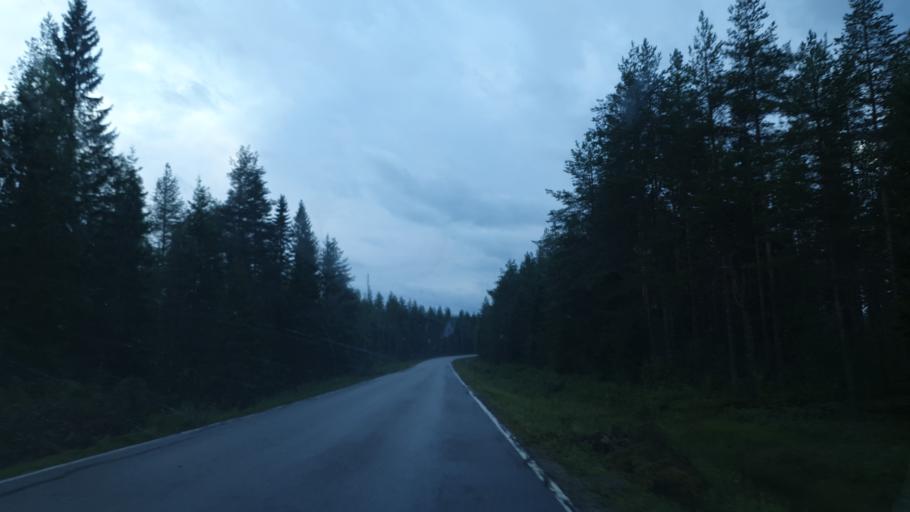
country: FI
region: Kainuu
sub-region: Kehys-Kainuu
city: Kuhmo
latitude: 63.9581
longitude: 29.7044
